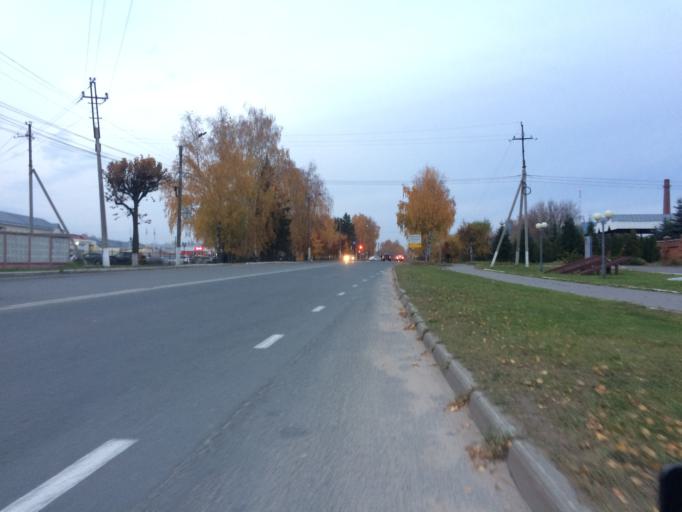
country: RU
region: Mariy-El
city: Yoshkar-Ola
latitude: 56.6070
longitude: 47.8804
